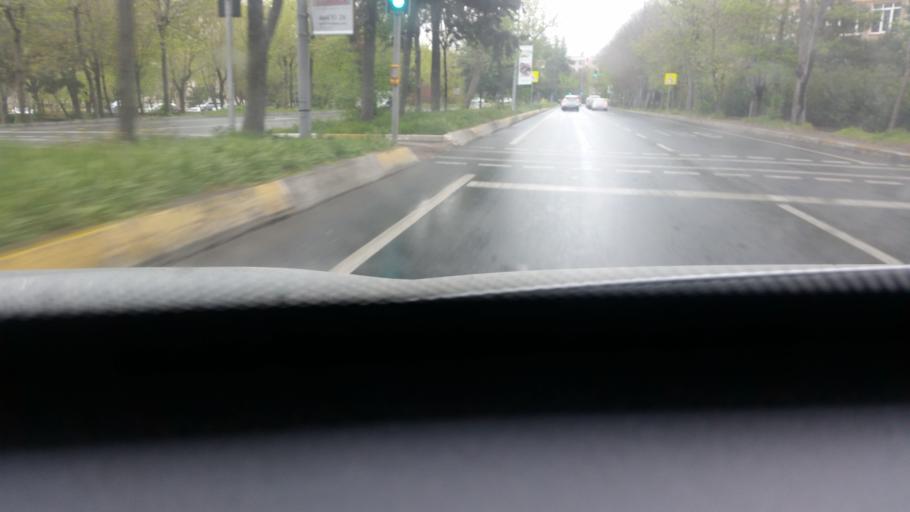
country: TR
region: Istanbul
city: Bahcelievler
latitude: 40.9821
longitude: 28.8523
